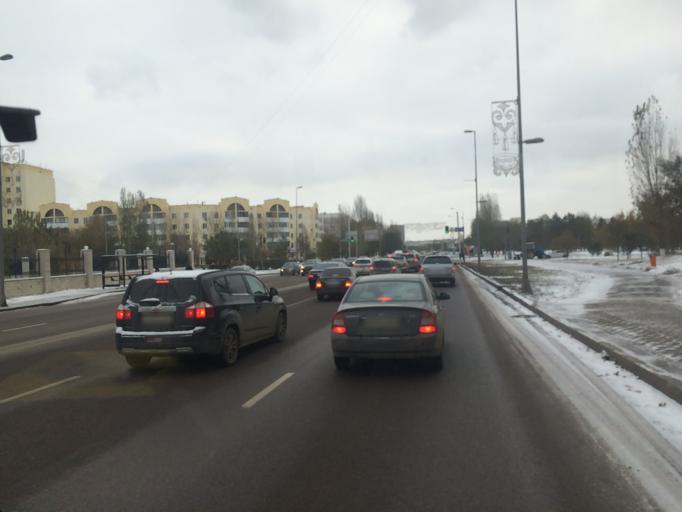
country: KZ
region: Astana Qalasy
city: Astana
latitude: 51.1520
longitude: 71.4362
